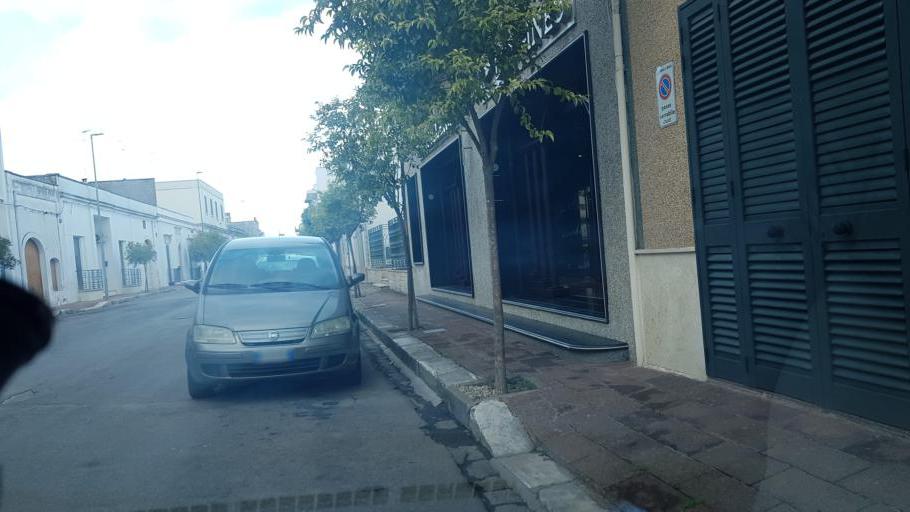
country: IT
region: Apulia
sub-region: Provincia di Lecce
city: Veglie
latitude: 40.3314
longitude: 17.9689
